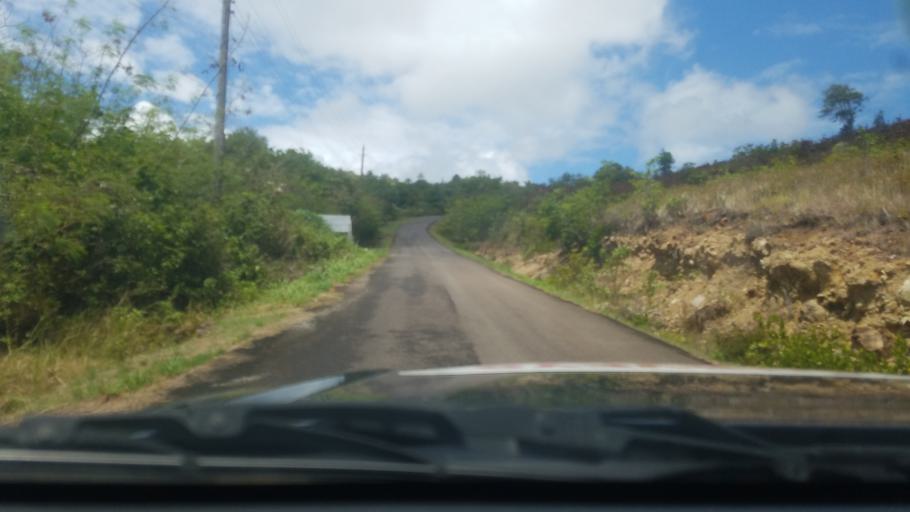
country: LC
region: Dennery Quarter
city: Dennery
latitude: 13.8993
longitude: -60.8922
